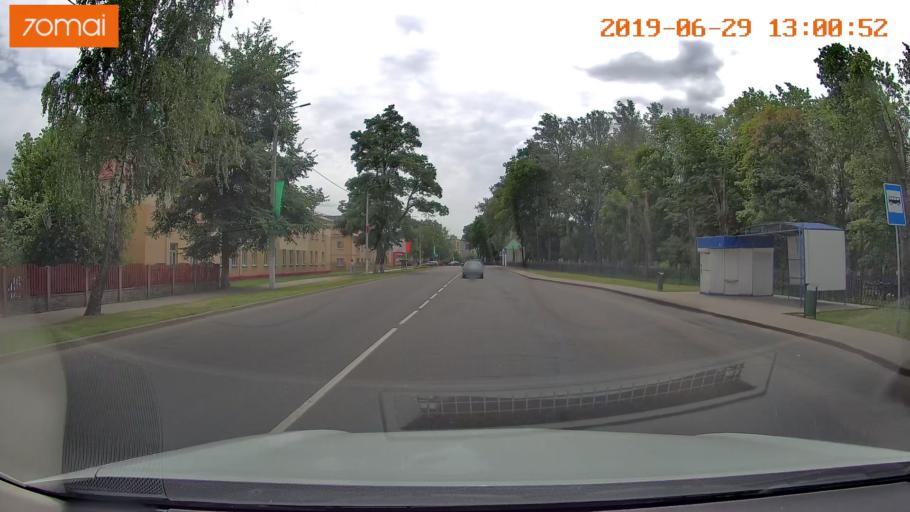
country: BY
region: Minsk
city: Slutsk
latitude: 53.0420
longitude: 27.5584
